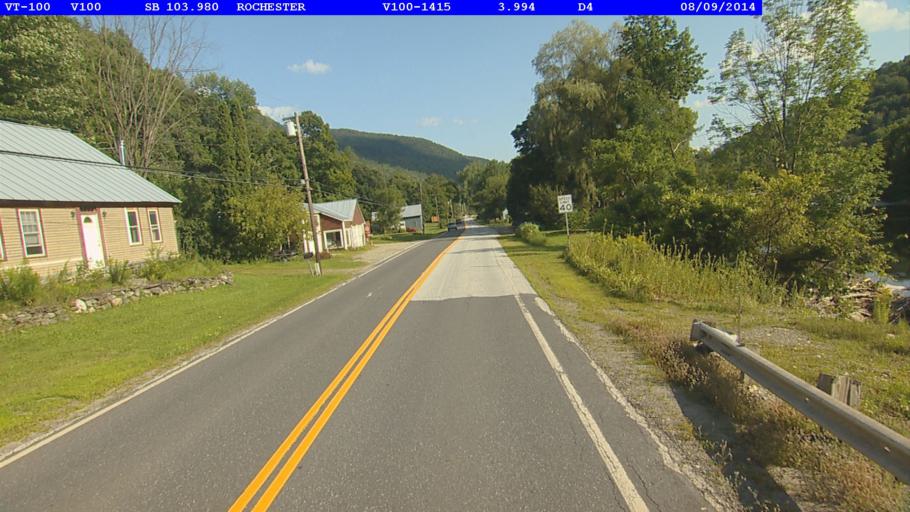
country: US
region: Vermont
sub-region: Orange County
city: Randolph
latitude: 43.8583
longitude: -72.8054
